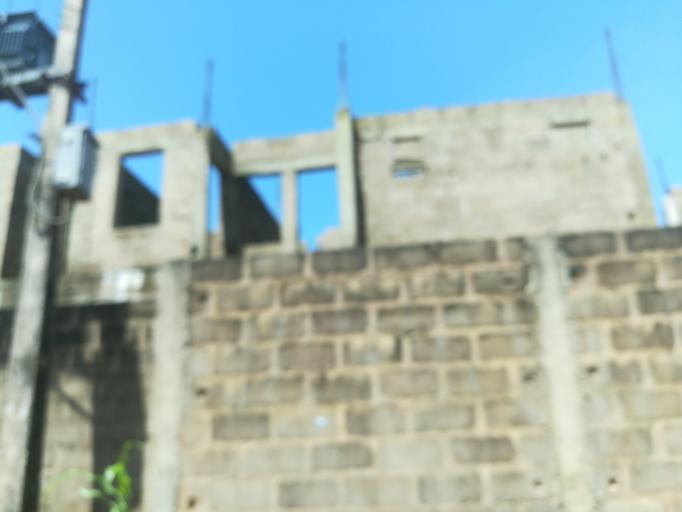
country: NG
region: Lagos
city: Oshodi
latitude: 6.5683
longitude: 3.3359
